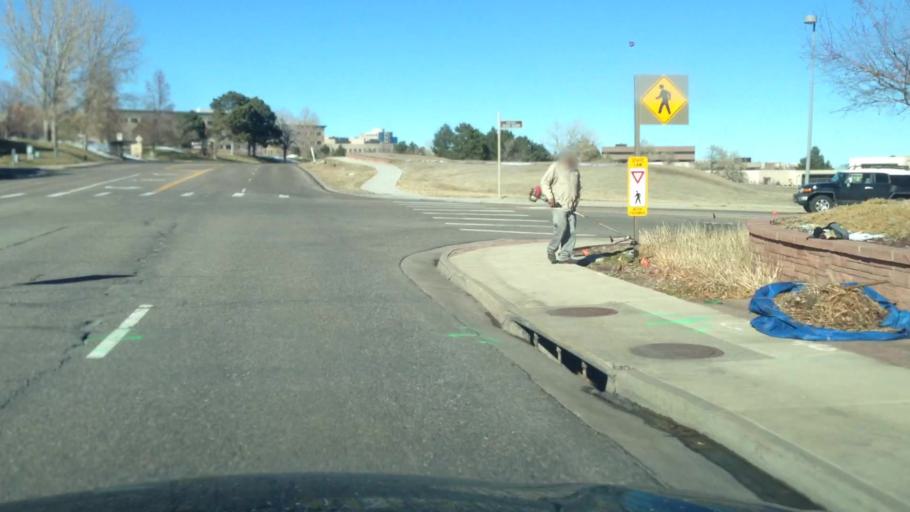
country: US
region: Colorado
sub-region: Douglas County
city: Meridian
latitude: 39.5594
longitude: -104.8650
